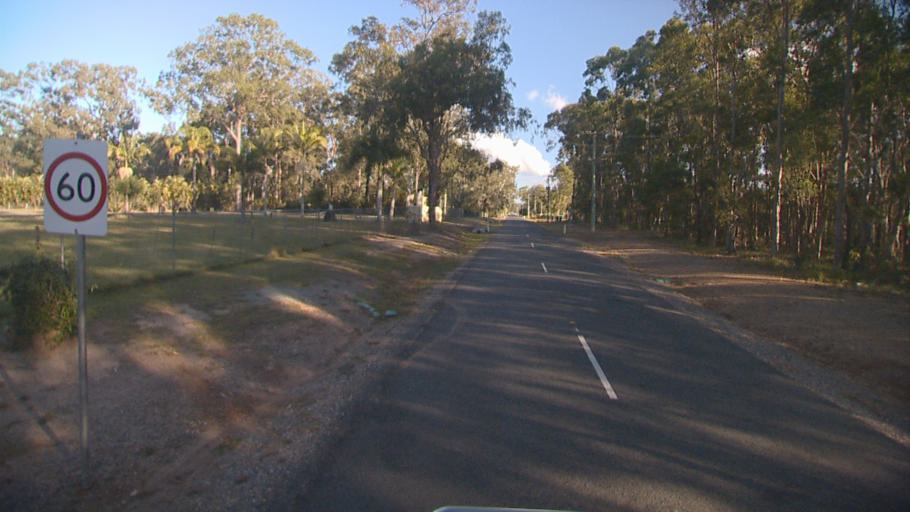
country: AU
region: Queensland
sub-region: Gold Coast
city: Yatala
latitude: -27.6706
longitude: 153.2441
